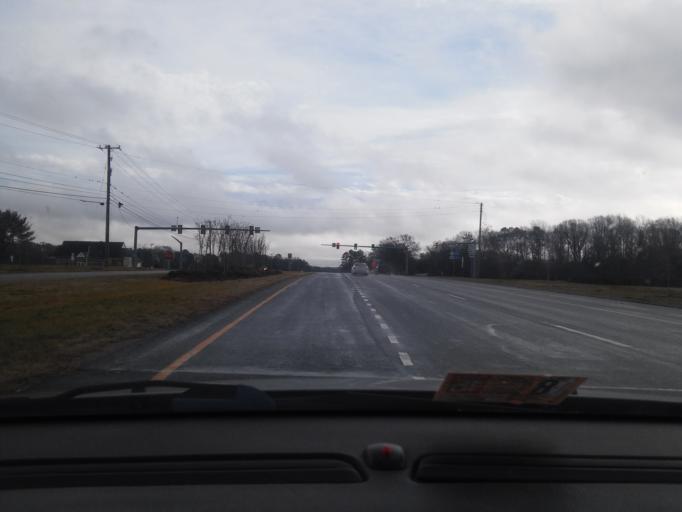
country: US
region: Virginia
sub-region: Henrico County
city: Short Pump
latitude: 37.6685
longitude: -77.6765
